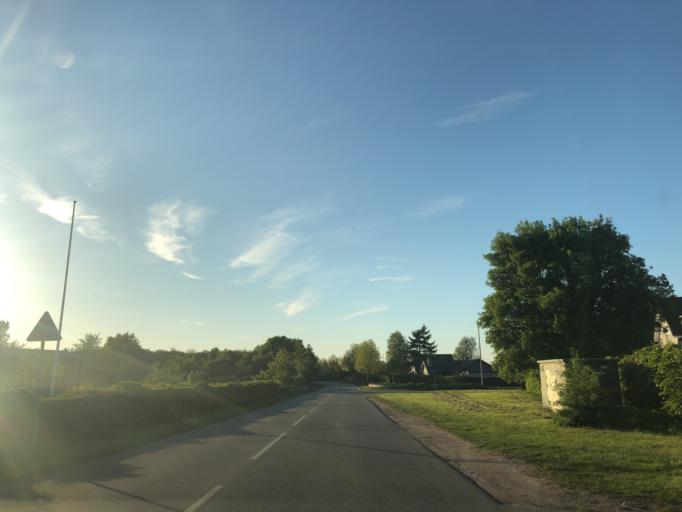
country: DK
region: Zealand
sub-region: Koge Kommune
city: Bjaeverskov
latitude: 55.4509
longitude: 12.0370
